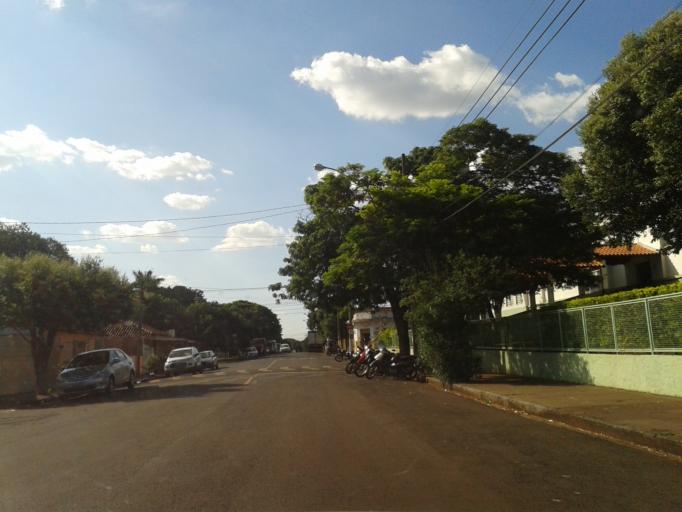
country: BR
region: Minas Gerais
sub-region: Ituiutaba
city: Ituiutaba
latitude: -18.9682
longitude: -49.4552
